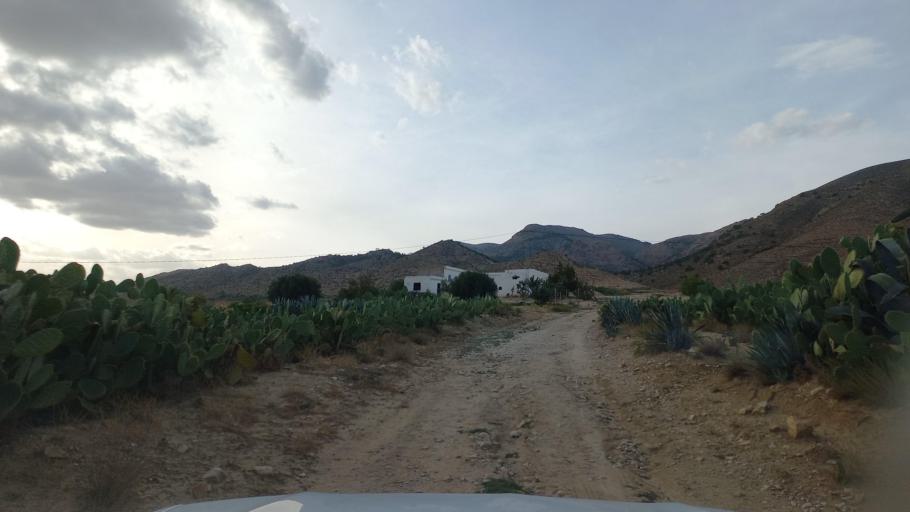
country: TN
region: Al Qasrayn
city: Sbiba
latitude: 35.4503
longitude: 9.0643
